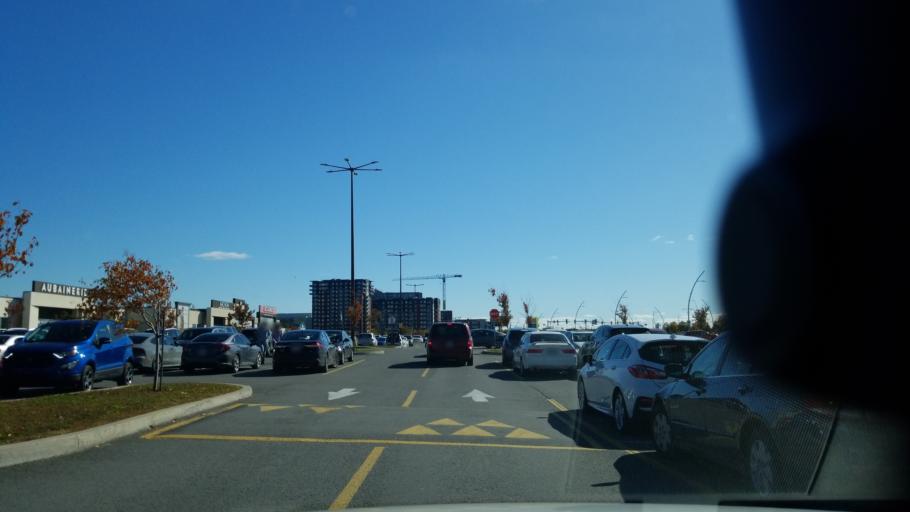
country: CA
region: Quebec
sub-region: Laval
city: Laval
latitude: 45.5643
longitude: -73.7304
